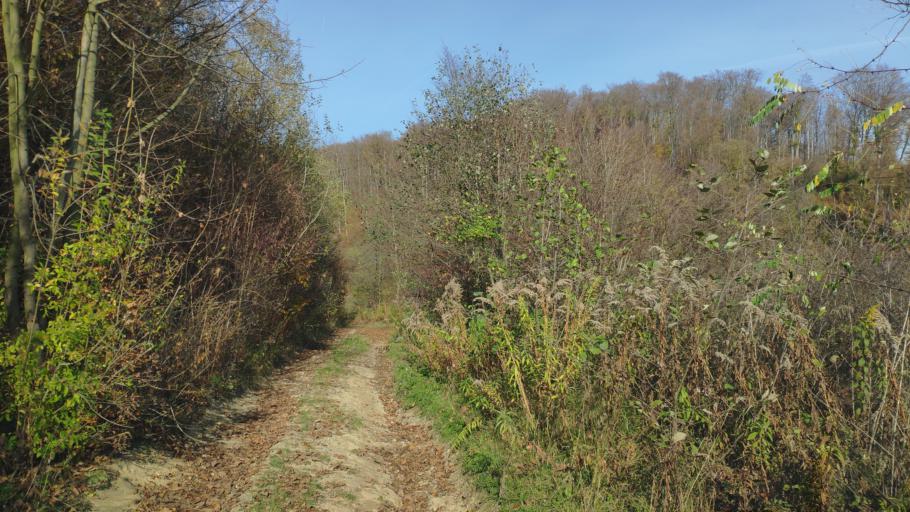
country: SK
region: Presovsky
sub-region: Okres Presov
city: Presov
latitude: 48.9027
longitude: 21.2220
